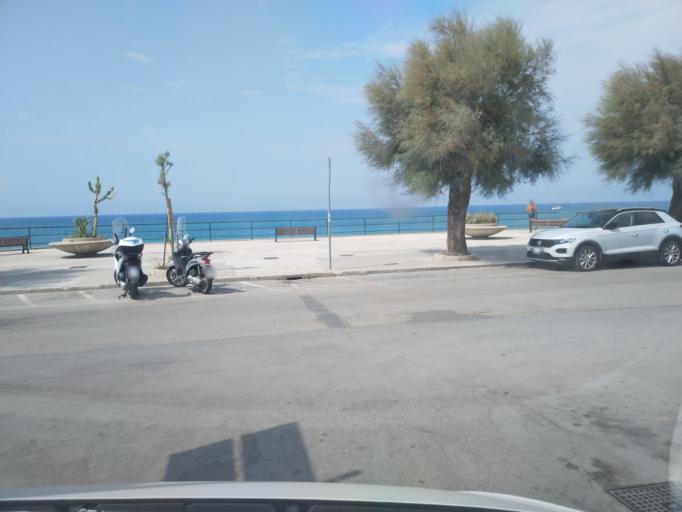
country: IT
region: Sicily
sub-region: Palermo
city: Cefalu
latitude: 38.0341
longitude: 14.0128
